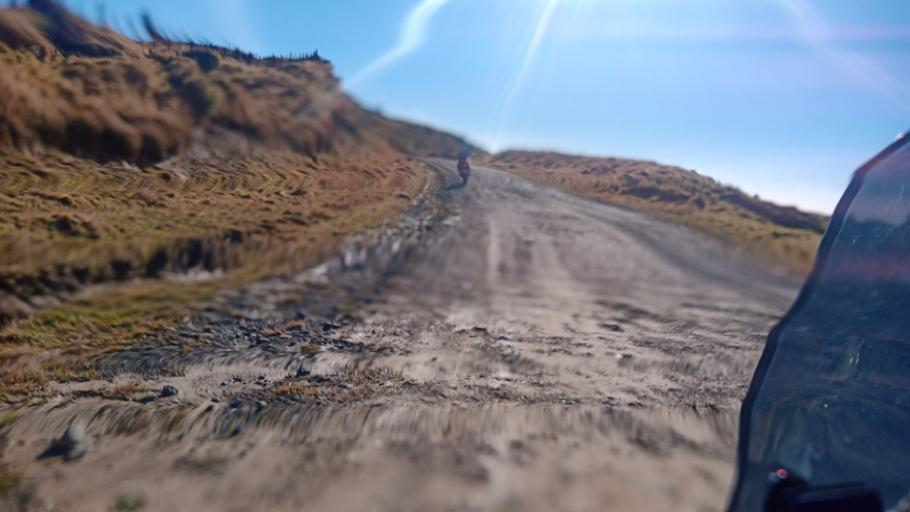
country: NZ
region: Gisborne
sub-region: Gisborne District
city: Gisborne
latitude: -38.1792
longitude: 177.8255
